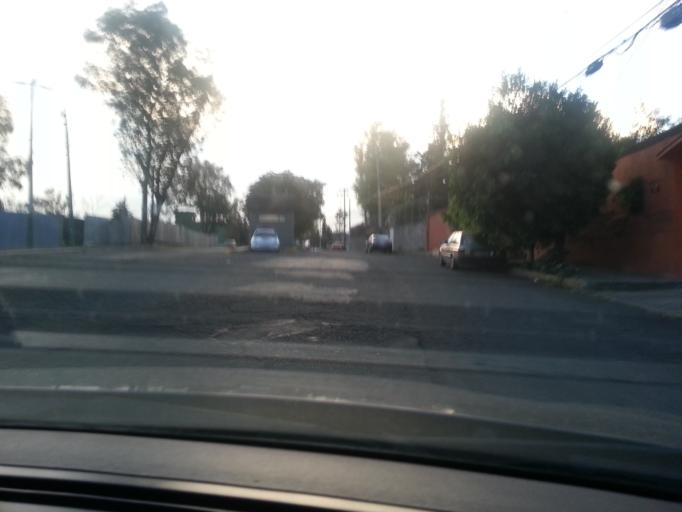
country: MX
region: Mexico
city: Ciudad Lopez Mateos
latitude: 19.6124
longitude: -99.2435
